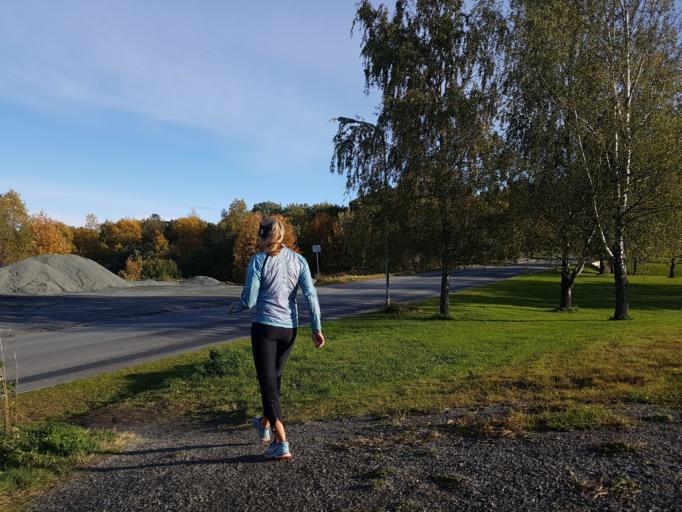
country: NO
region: Sor-Trondelag
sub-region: Trondheim
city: Trondheim
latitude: 63.4245
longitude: 10.3548
